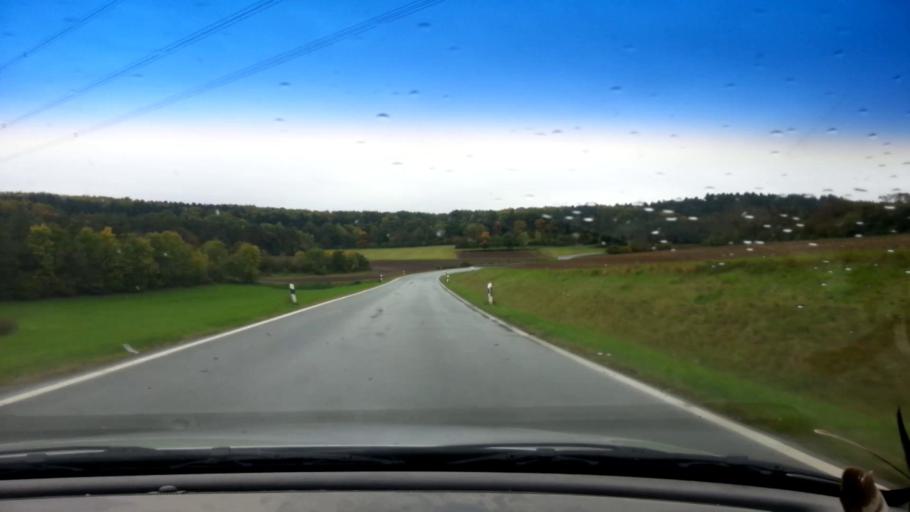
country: DE
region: Bavaria
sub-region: Upper Franconia
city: Poxdorf
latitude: 49.8799
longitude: 11.1057
